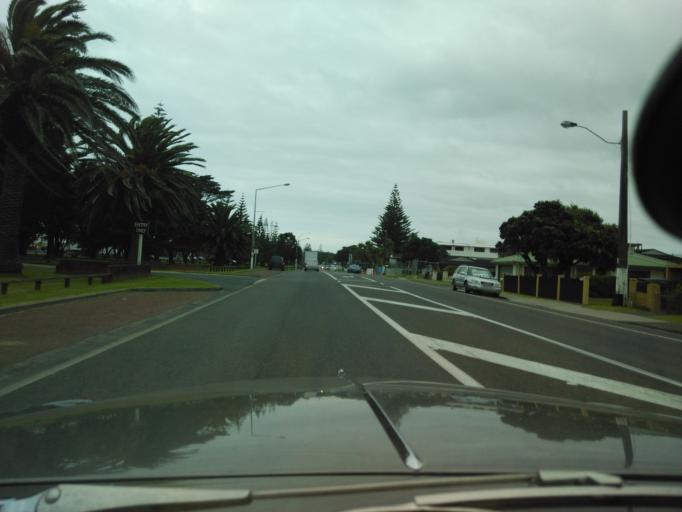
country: NZ
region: Auckland
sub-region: Auckland
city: Rothesay Bay
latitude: -36.5910
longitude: 174.6982
